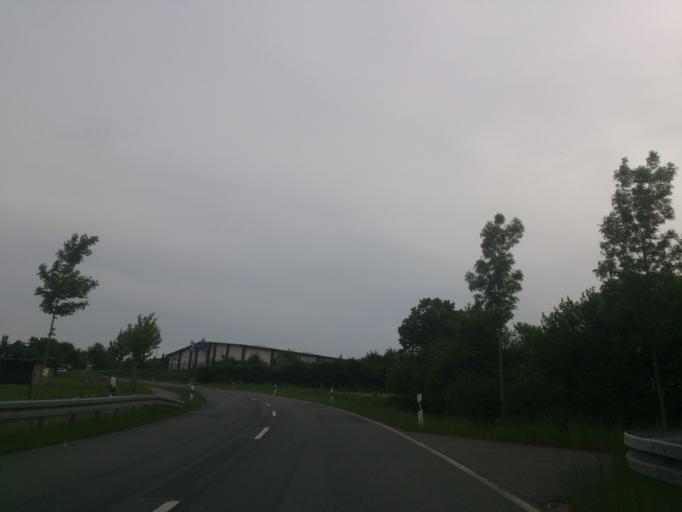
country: DE
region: North Rhine-Westphalia
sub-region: Regierungsbezirk Detmold
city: Altenbeken
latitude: 51.7449
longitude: 8.9507
